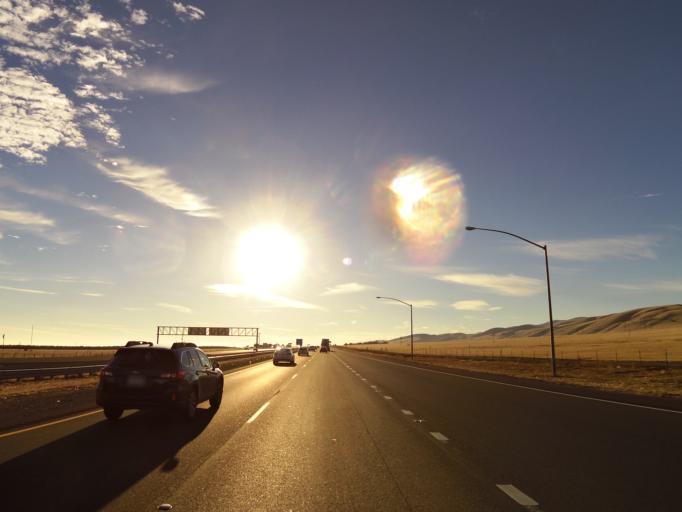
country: US
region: California
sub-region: San Joaquin County
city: Tracy
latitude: 37.5906
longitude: -121.3335
